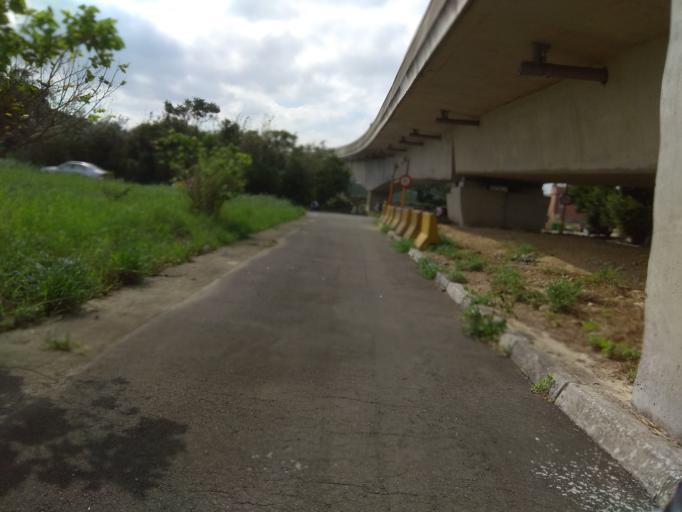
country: TW
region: Taiwan
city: Taoyuan City
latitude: 25.0613
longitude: 121.2118
